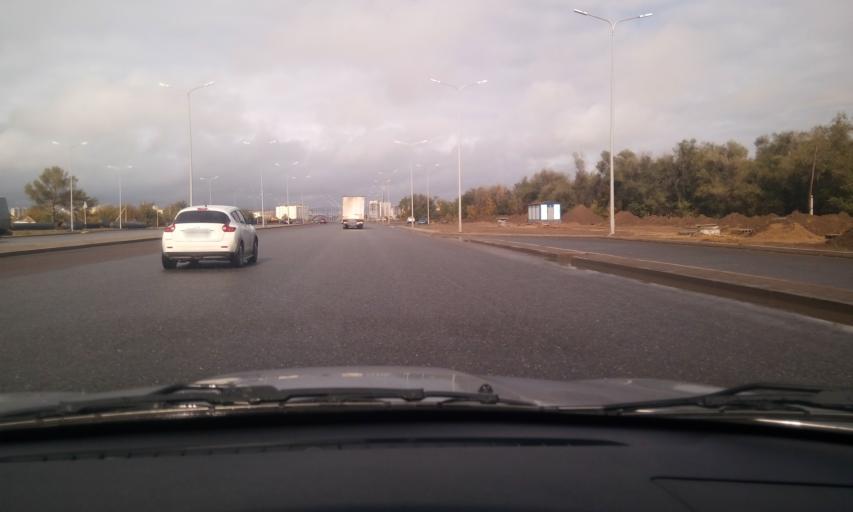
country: KZ
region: Astana Qalasy
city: Astana
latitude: 51.1564
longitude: 71.3721
